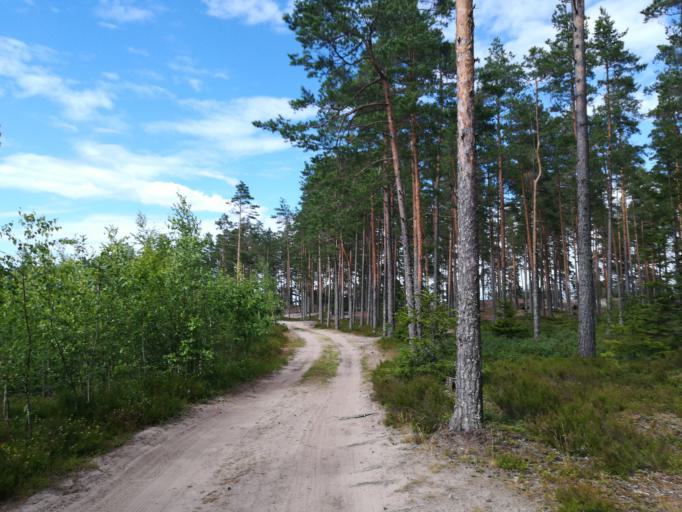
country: RU
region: Leningrad
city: Ust'-Luga
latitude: 59.6798
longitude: 28.2294
